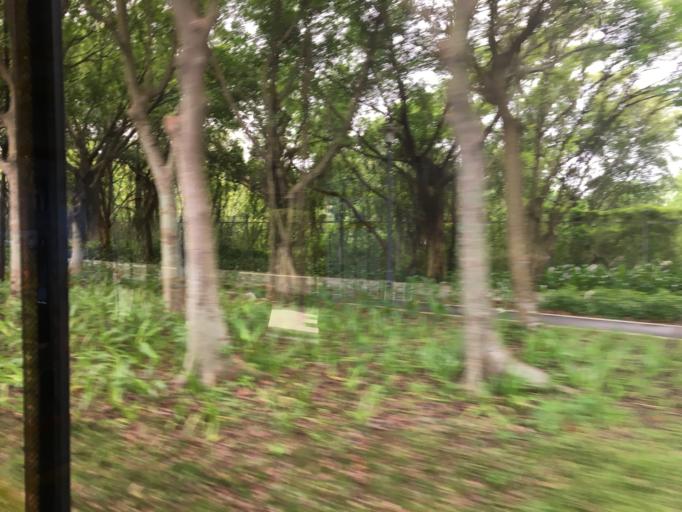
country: CN
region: Guangdong
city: Shahe
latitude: 22.5286
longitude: 113.9787
